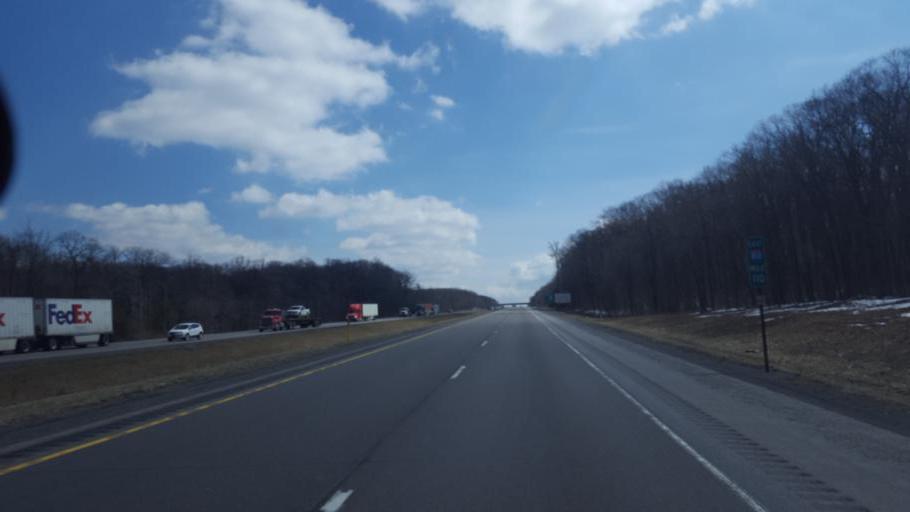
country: US
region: Pennsylvania
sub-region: Clearfield County
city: Clearfield
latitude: 41.1145
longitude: -78.5448
